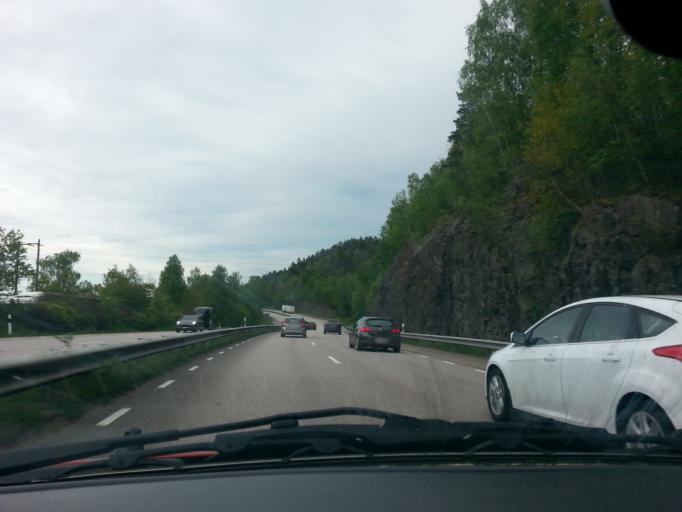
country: SE
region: Vaestra Goetaland
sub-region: Alingsas Kommun
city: Ingared
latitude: 57.8227
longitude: 12.4223
